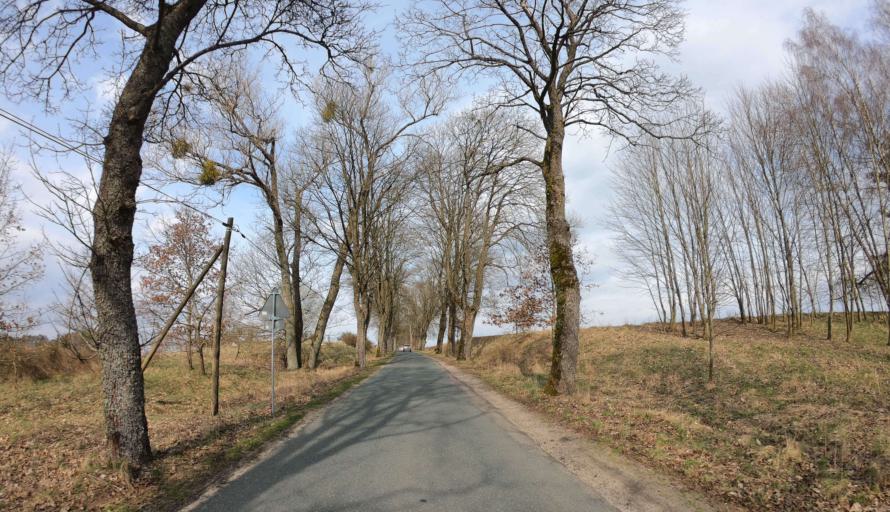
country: PL
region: West Pomeranian Voivodeship
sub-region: Powiat swidwinski
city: Swidwin
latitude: 53.8270
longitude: 15.8255
